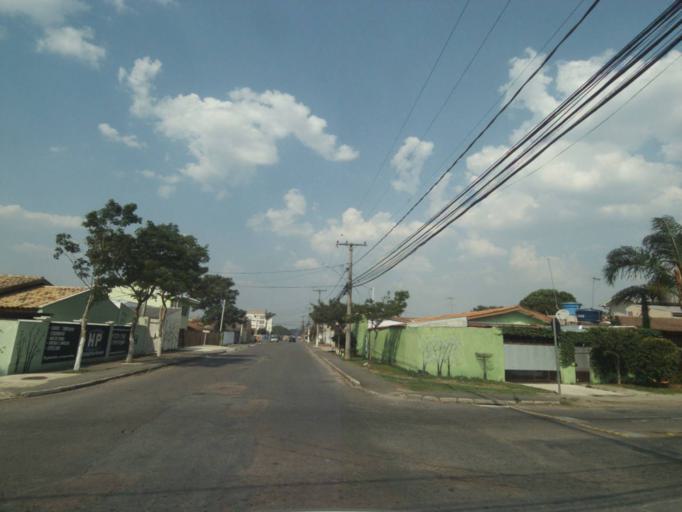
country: BR
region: Parana
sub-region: Sao Jose Dos Pinhais
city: Sao Jose dos Pinhais
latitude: -25.5360
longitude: -49.2409
